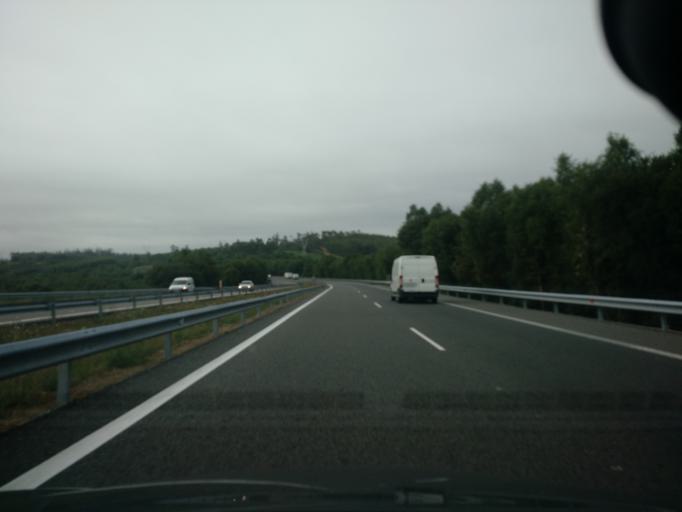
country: ES
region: Galicia
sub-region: Provincia da Coruna
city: Mesia
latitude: 43.1373
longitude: -8.3304
